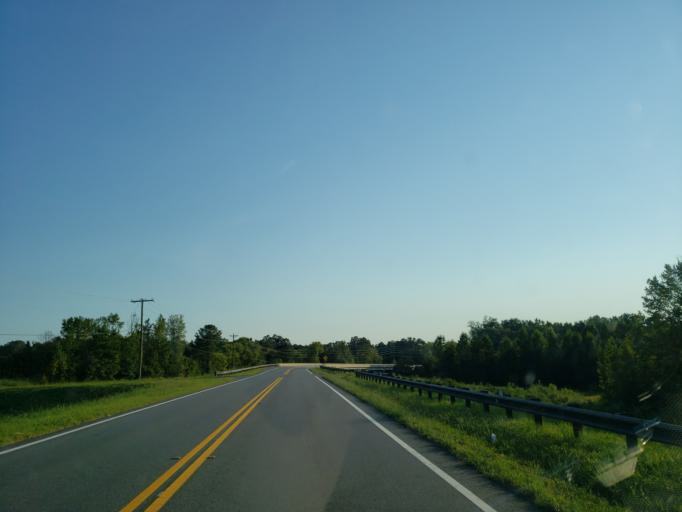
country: US
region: Georgia
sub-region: Gordon County
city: Calhoun
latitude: 34.5439
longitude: -84.8986
